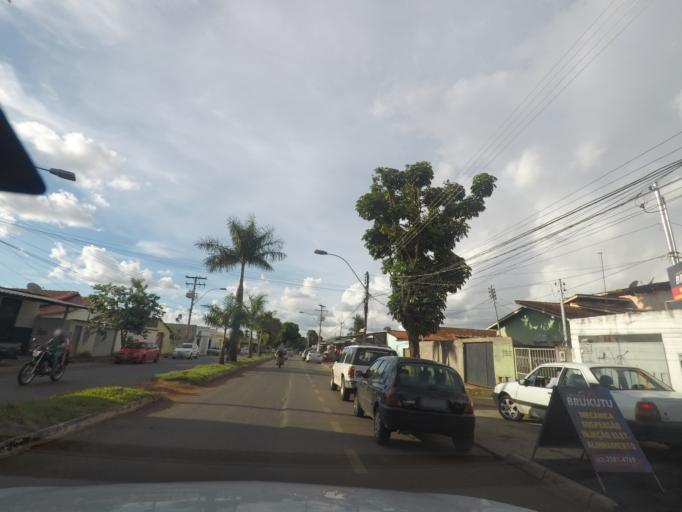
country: BR
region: Goias
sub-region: Goiania
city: Goiania
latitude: -16.6769
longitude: -49.3118
